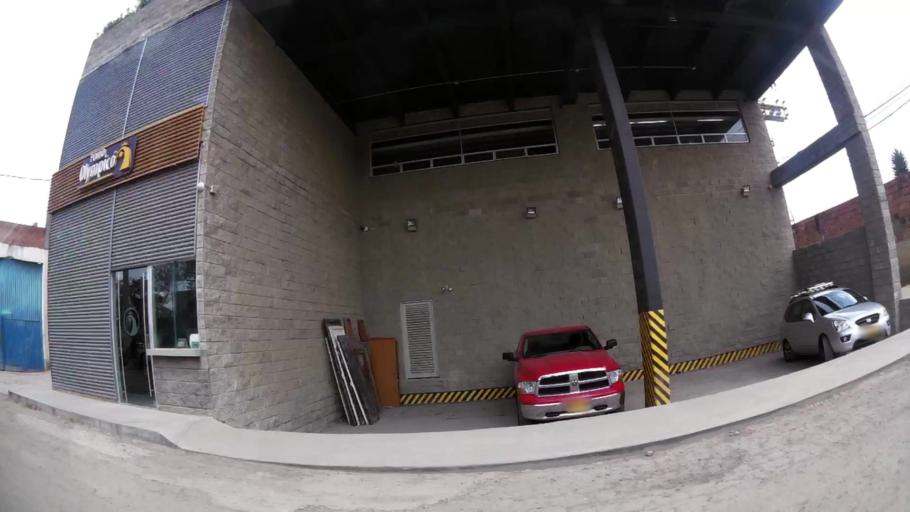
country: CO
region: Bogota D.C.
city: Bogota
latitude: 4.6533
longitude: -74.1332
